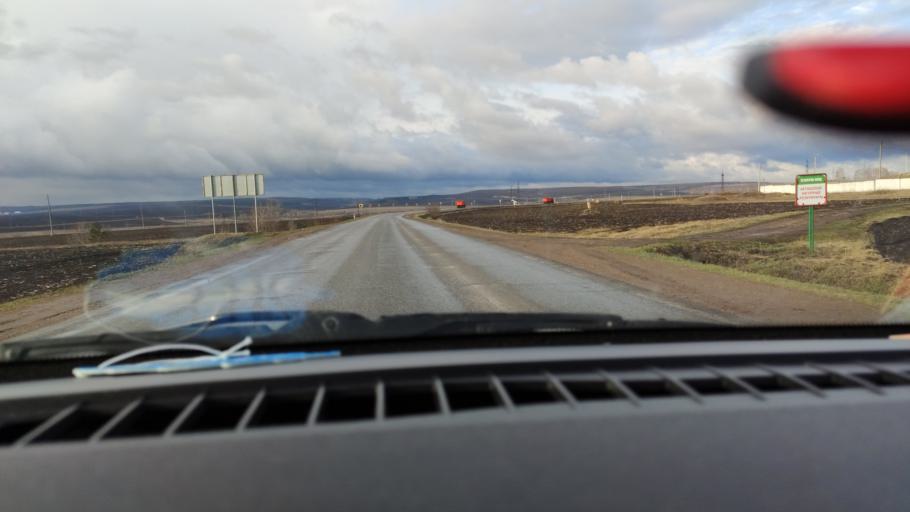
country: RU
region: Tatarstan
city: Russkiy Aktash
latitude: 55.0434
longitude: 52.0930
